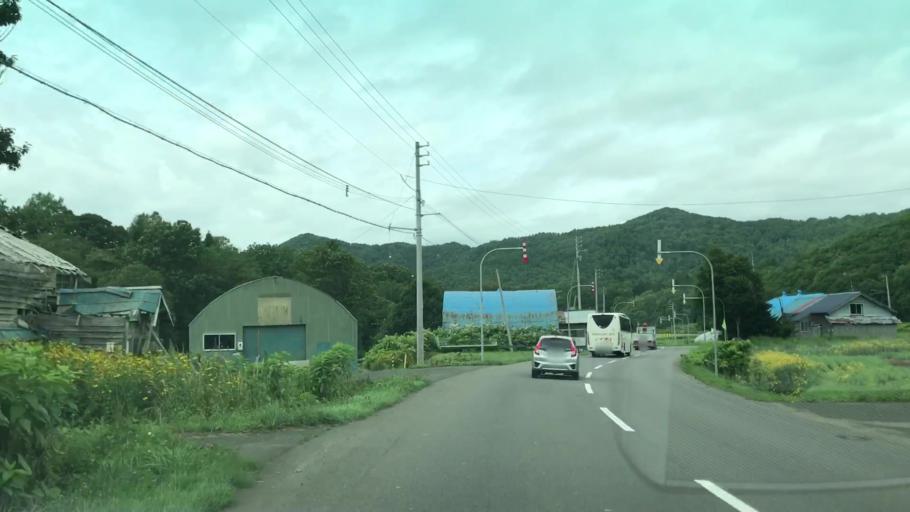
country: JP
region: Hokkaido
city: Niseko Town
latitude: 42.9479
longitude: 140.8331
